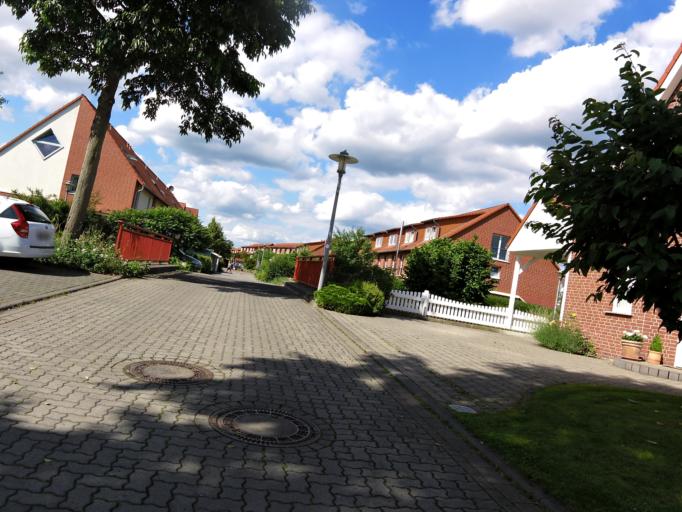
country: DE
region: Lower Saxony
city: Goettingen
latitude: 51.5079
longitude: 9.9468
